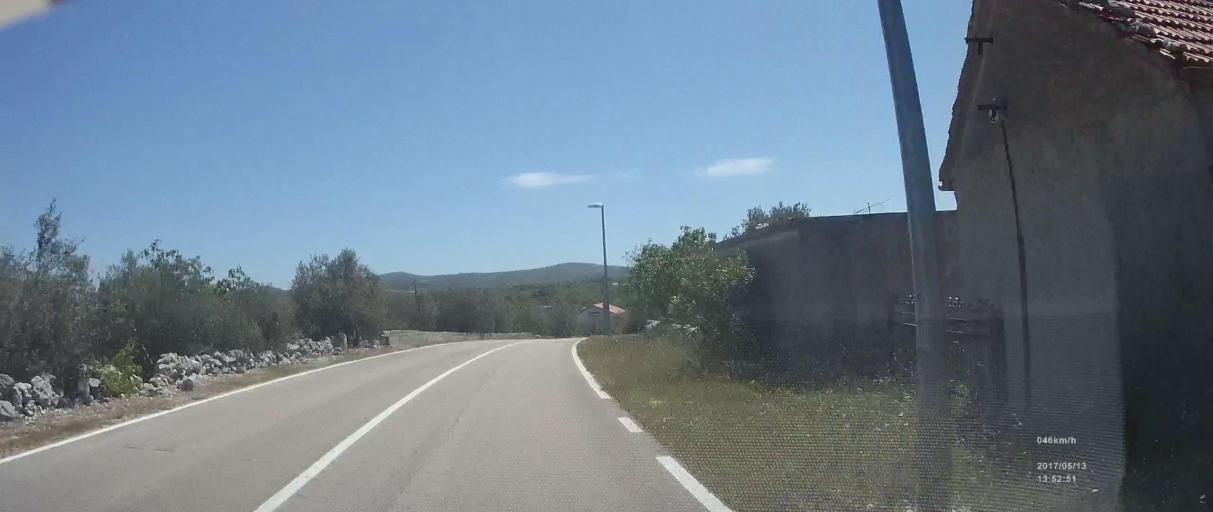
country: HR
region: Sibensko-Kniniska
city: Primosten
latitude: 43.6036
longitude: 15.9967
